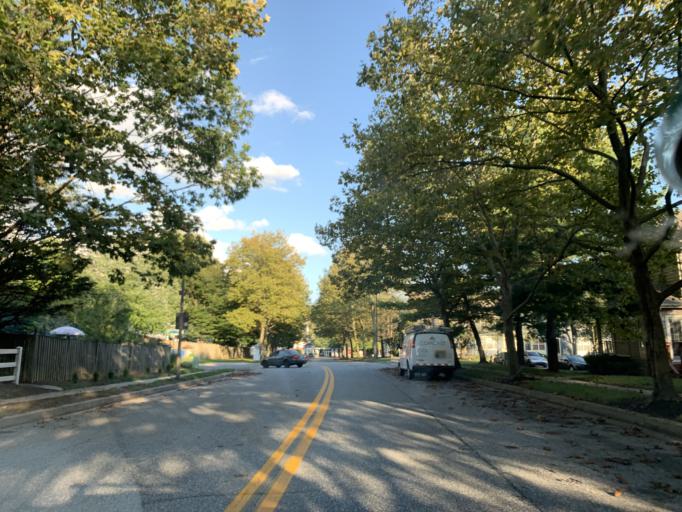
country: US
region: Maryland
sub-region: Baltimore County
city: Owings Mills
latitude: 39.4053
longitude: -76.8070
